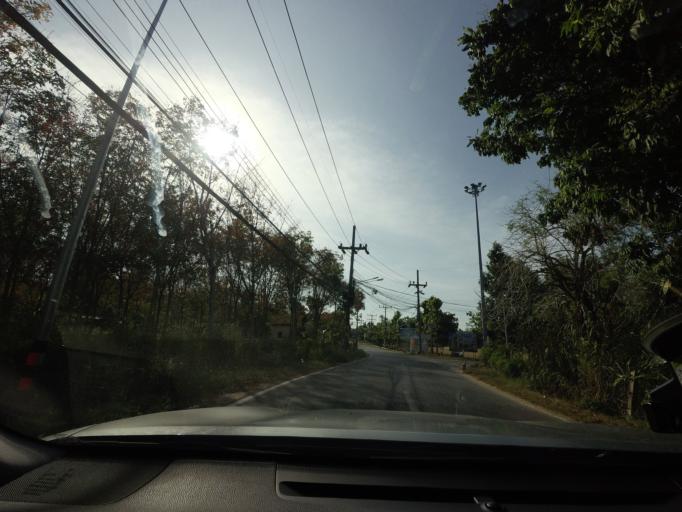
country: TH
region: Phuket
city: Thalang
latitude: 8.0183
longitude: 98.3087
